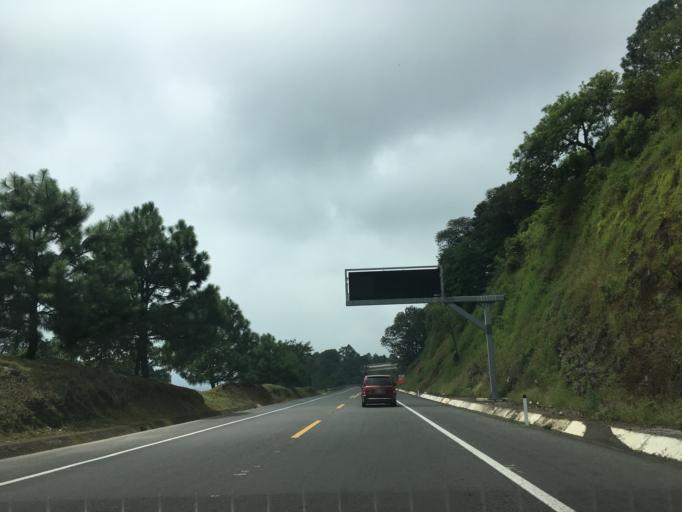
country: MX
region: Michoacan
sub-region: Ziracuaretiro
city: Patuan
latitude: 19.4355
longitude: -101.8898
